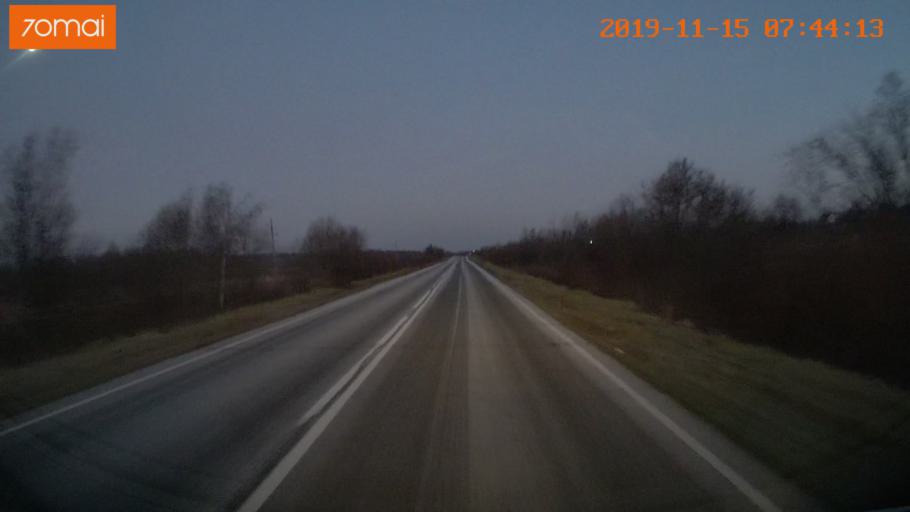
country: RU
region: Vologda
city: Sheksna
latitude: 58.8111
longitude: 38.3162
